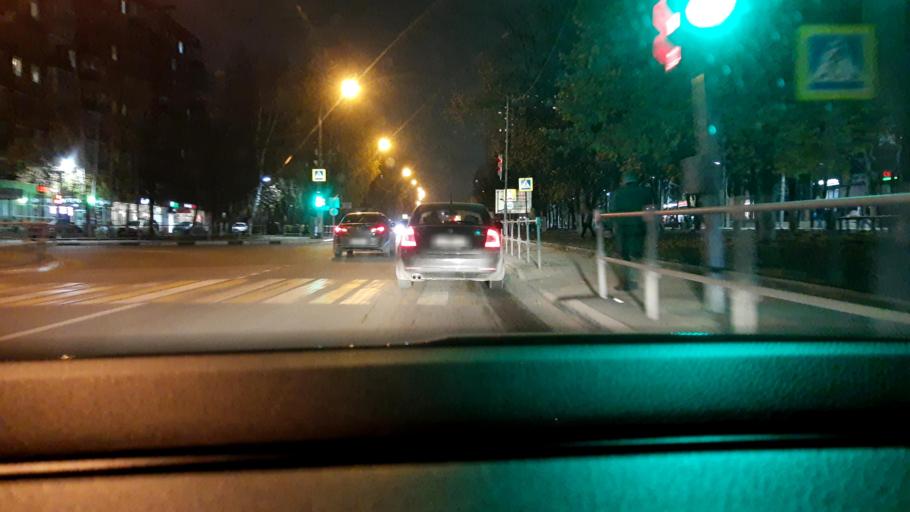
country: RU
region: Moskovskaya
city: Dolgoprudnyy
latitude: 55.9412
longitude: 37.5092
